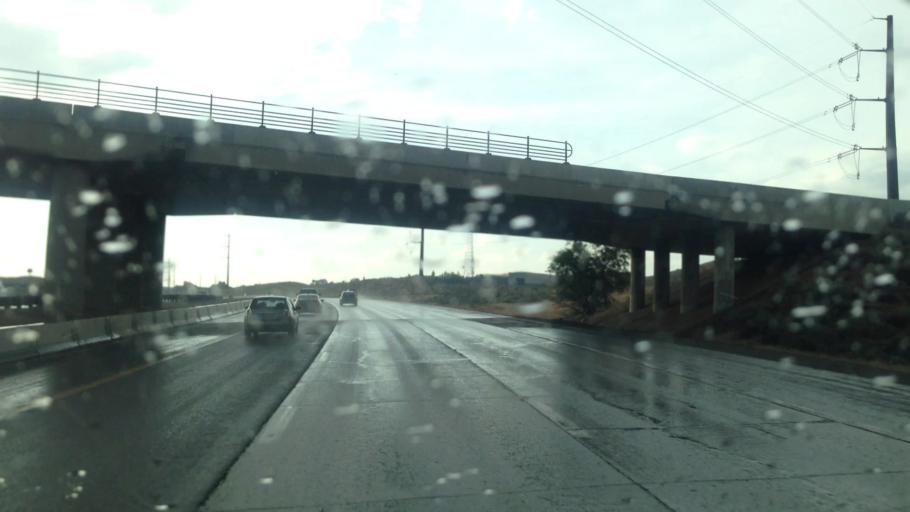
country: US
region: Nevada
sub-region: Washoe County
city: Sun Valley
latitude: 39.5725
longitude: -119.8087
